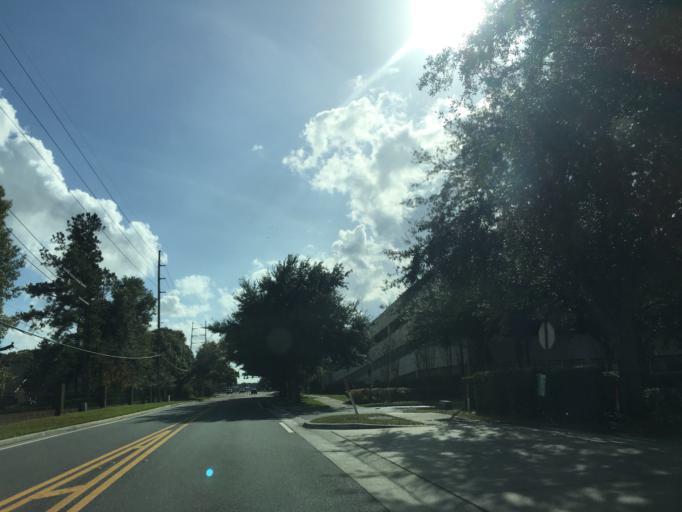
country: US
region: Florida
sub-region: Orange County
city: Eatonville
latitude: 28.6386
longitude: -81.3986
